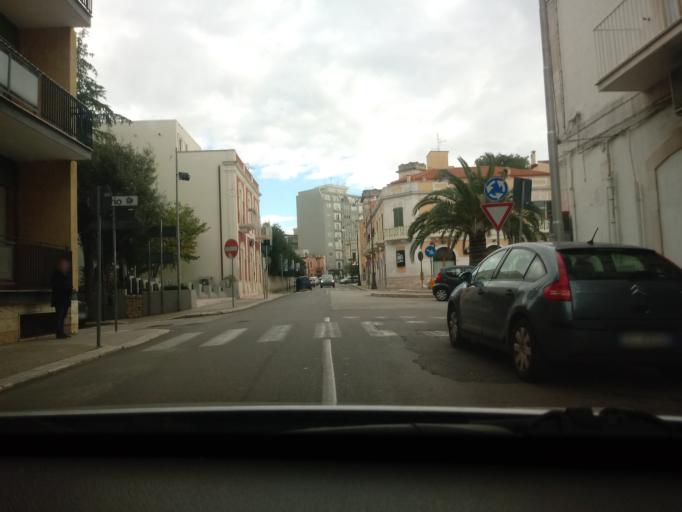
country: IT
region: Apulia
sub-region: Provincia di Bari
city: Putignano
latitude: 40.8531
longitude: 17.1183
